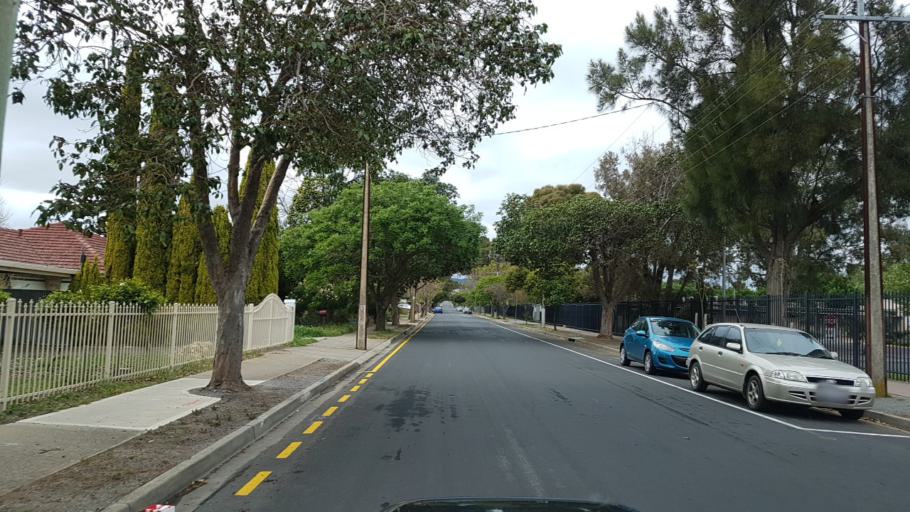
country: AU
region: South Australia
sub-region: Norwood Payneham St Peters
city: Marden
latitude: -34.8901
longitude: 138.6363
